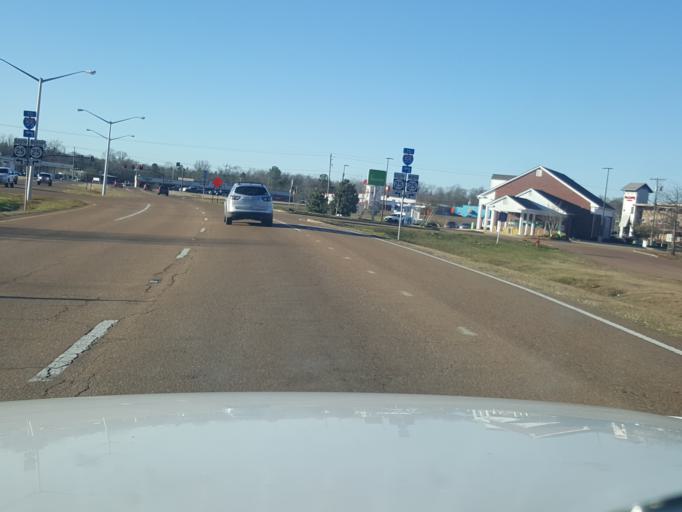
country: US
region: Mississippi
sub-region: Rankin County
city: Flowood
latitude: 32.3360
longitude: -90.0912
